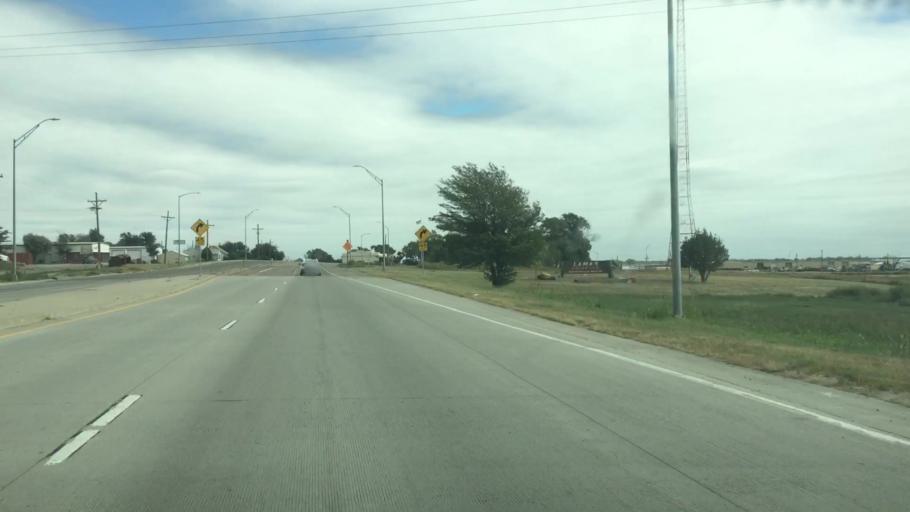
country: US
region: Colorado
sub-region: Prowers County
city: Lamar
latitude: 38.1153
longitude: -102.6237
